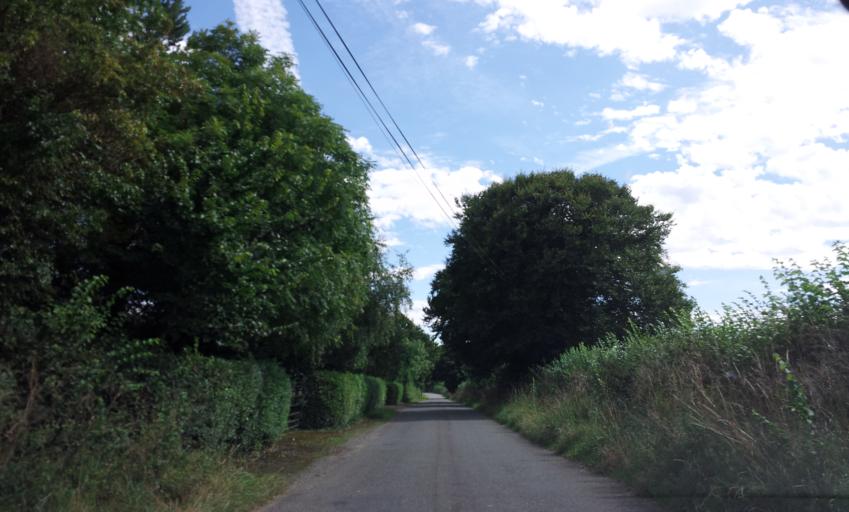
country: IE
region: Leinster
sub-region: Kildare
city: Moone
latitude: 52.9850
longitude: -6.8404
